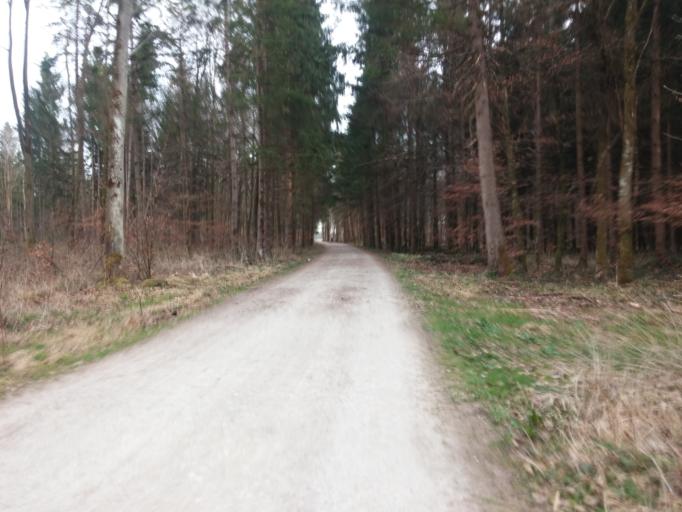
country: DE
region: Bavaria
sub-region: Upper Bavaria
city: Vaterstetten
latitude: 48.0819
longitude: 11.7697
